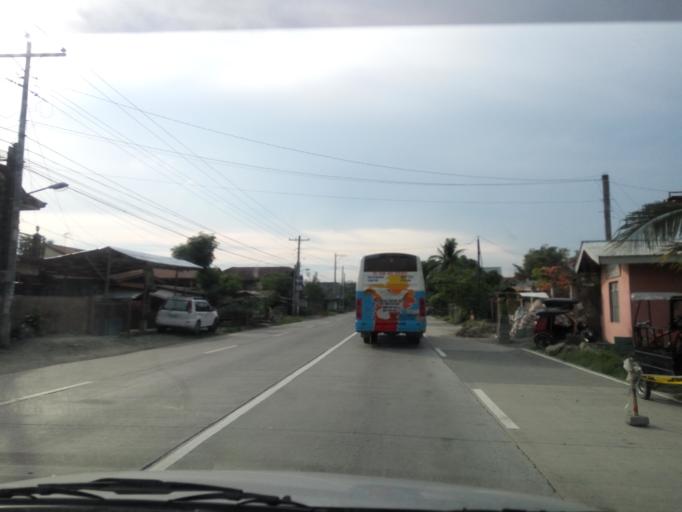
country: PH
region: Ilocos
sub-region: Province of Pangasinan
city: Pozorrubio
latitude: 16.0990
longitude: 120.5717
